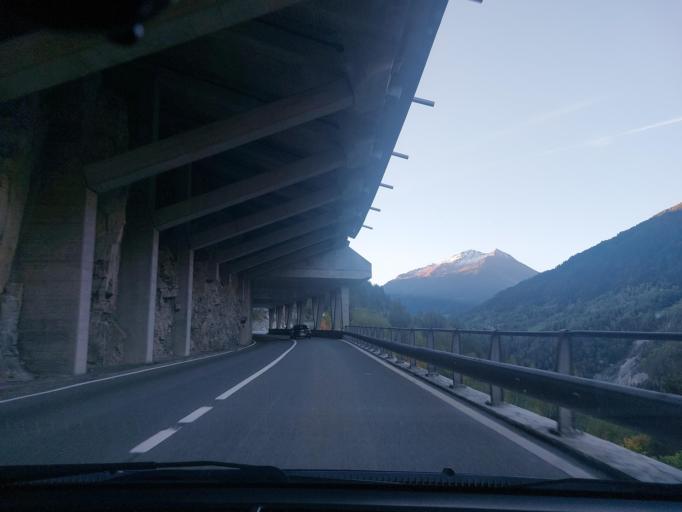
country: CH
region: Valais
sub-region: Sierre District
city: Chippis
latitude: 46.2300
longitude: 7.5798
